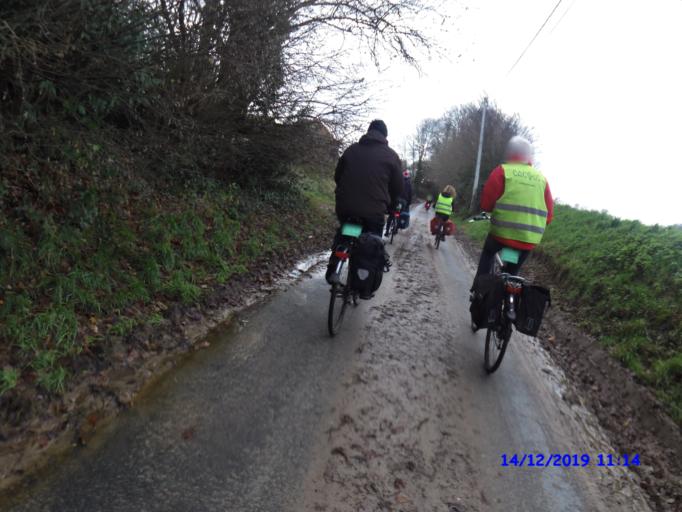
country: BE
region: Flanders
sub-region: Provincie Vlaams-Brabant
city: Beersel
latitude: 50.7458
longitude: 4.3134
